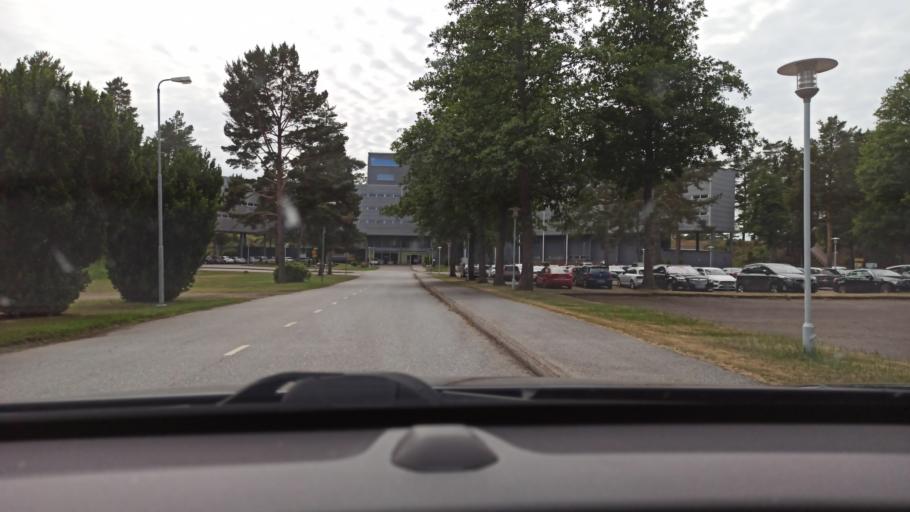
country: FI
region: Satakunta
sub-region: Pori
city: Luvia
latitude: 61.5713
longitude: 21.5198
